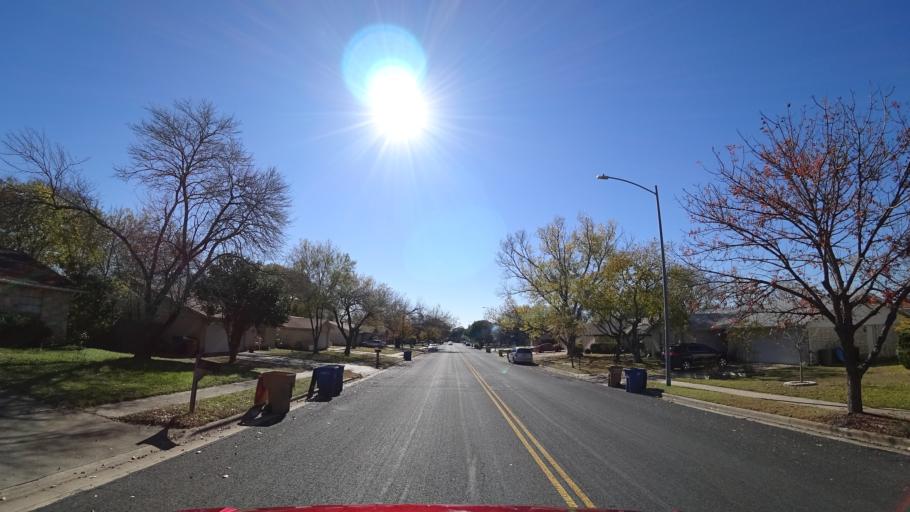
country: US
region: Texas
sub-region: Travis County
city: Wells Branch
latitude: 30.4230
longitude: -97.6924
